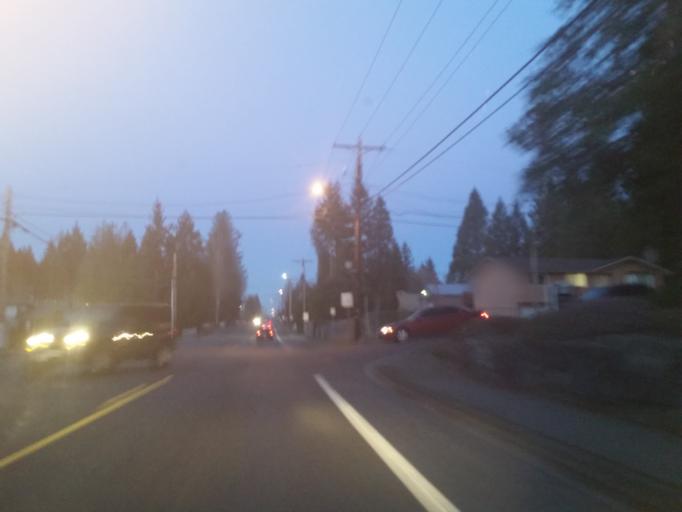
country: US
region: Washington
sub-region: Snohomish County
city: Meadowdale
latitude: 47.8753
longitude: -122.2905
